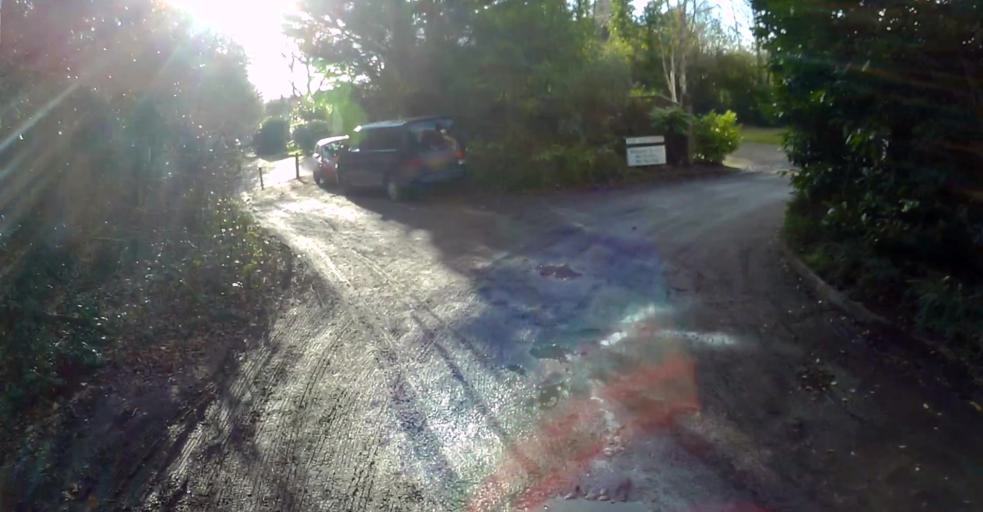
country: GB
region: England
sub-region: Surrey
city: Ottershaw
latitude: 51.3642
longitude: -0.5195
